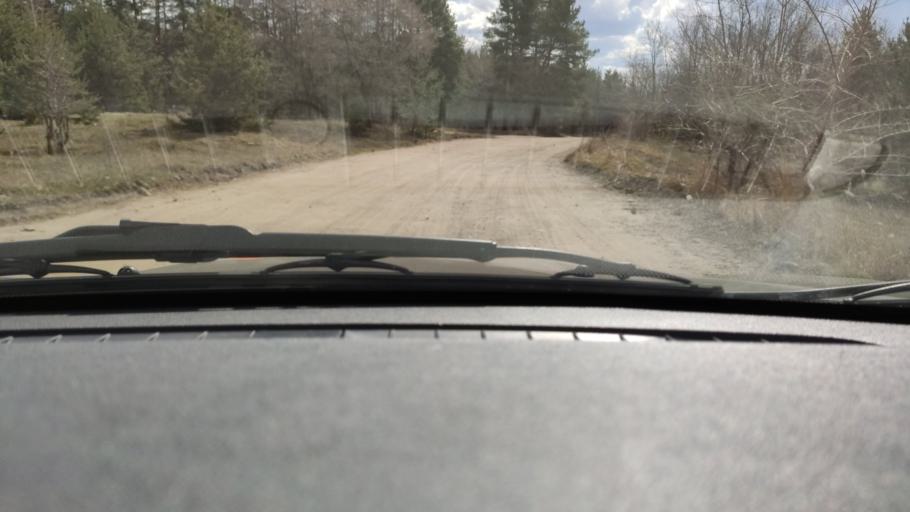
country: RU
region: Voronezj
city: Shilovo
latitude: 51.5578
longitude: 39.1155
